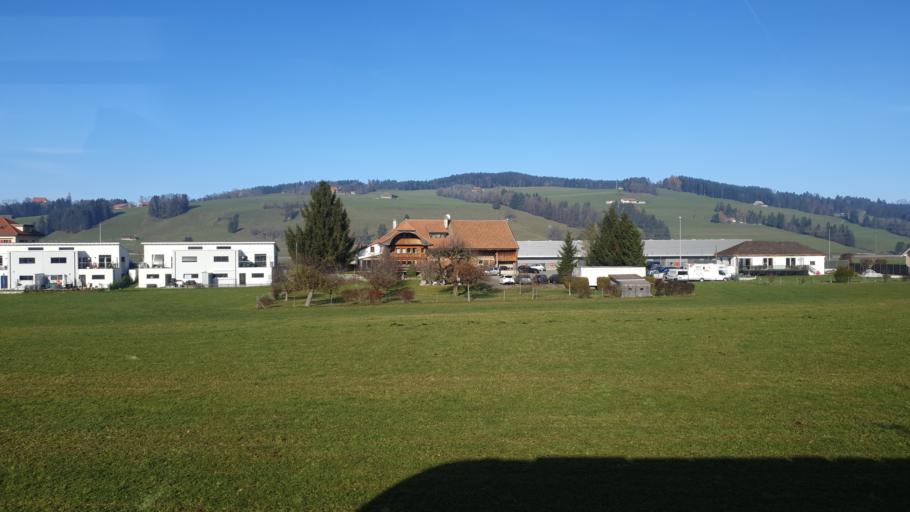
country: CH
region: Fribourg
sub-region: Gruyere District
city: Vuadens
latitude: 46.6175
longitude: 7.0150
